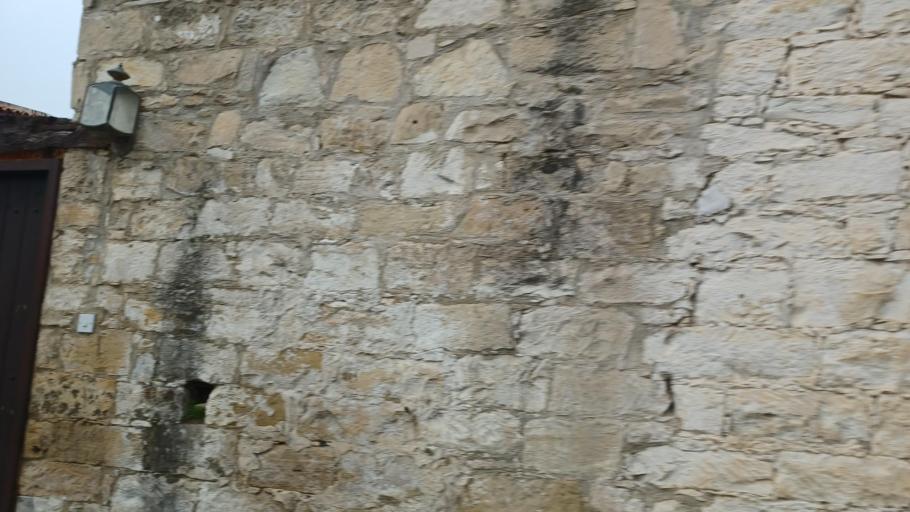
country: CY
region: Limassol
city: Pachna
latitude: 34.7388
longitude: 32.7333
